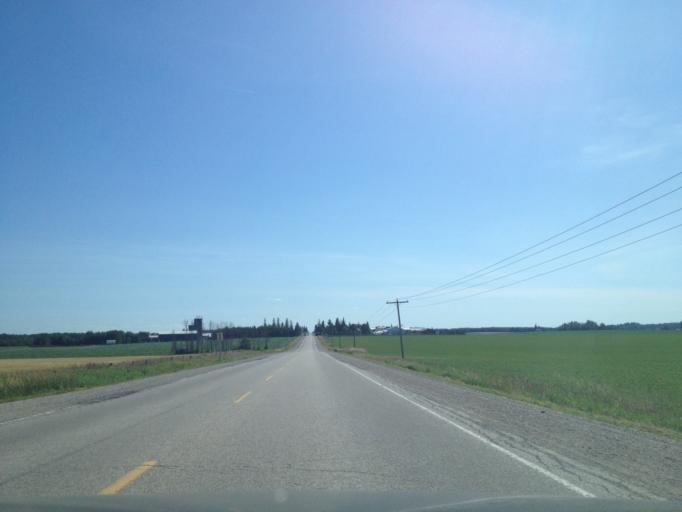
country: CA
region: Ontario
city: Waterloo
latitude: 43.5250
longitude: -80.7461
